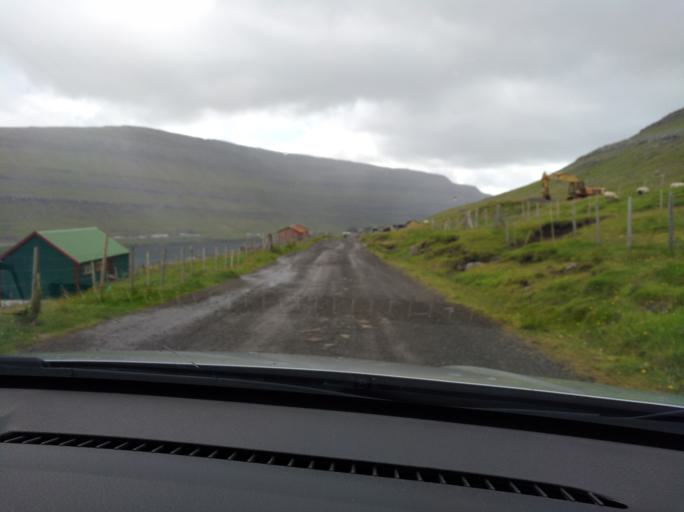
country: FO
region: Nordoyar
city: Klaksvik
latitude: 62.2201
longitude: -6.5893
